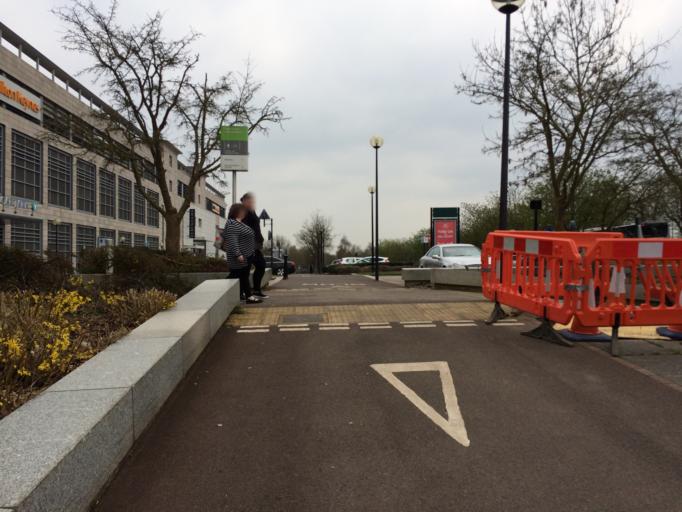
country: GB
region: England
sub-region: Milton Keynes
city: Milton Keynes
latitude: 52.0407
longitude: -0.7587
